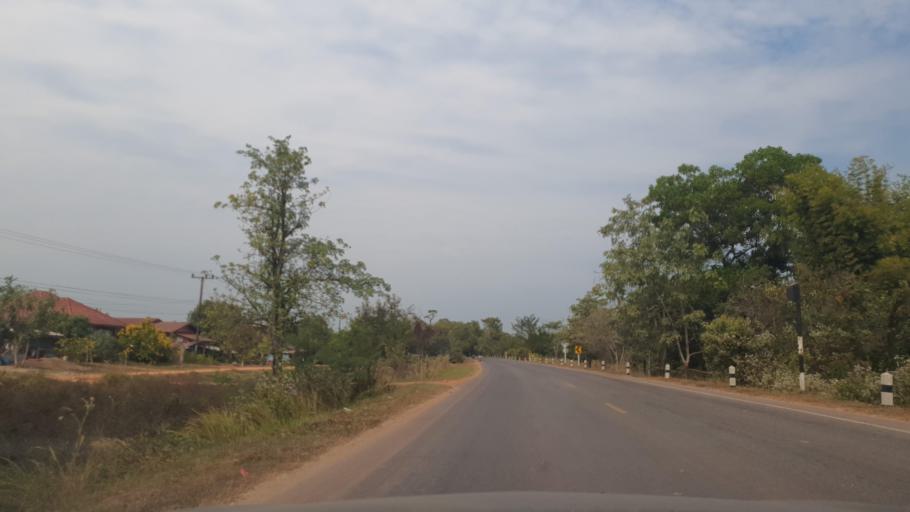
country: TH
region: Changwat Bueng Kan
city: Bung Khla
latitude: 18.2020
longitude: 104.0512
